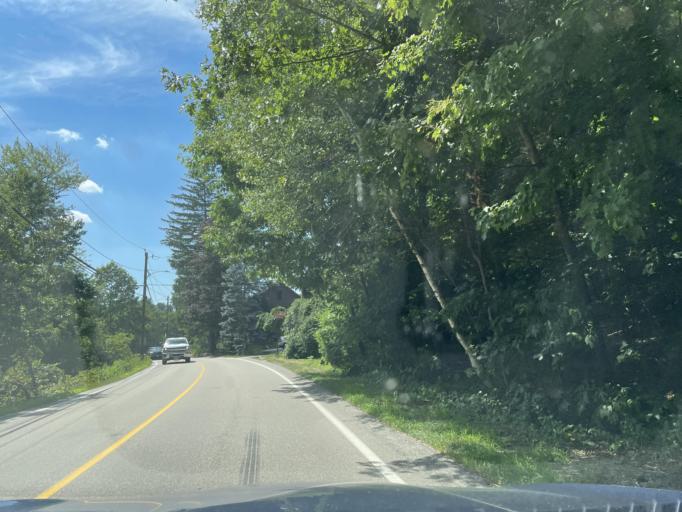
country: US
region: Massachusetts
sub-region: Middlesex County
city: Sherborn
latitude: 42.2376
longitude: -71.3942
